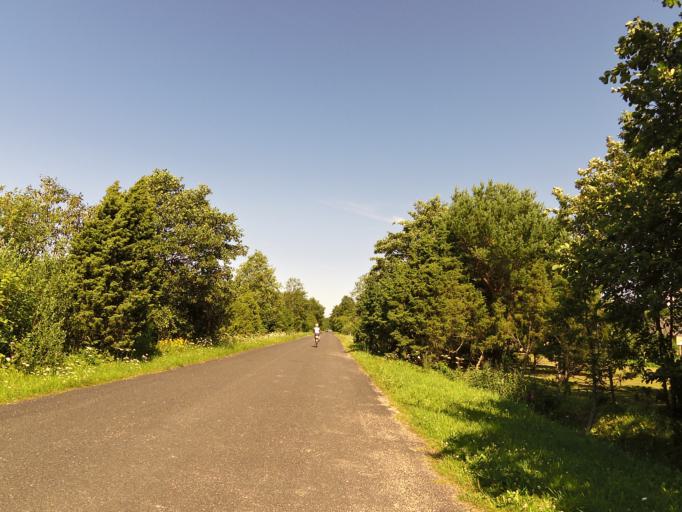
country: EE
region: Hiiumaa
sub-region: Kaerdla linn
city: Kardla
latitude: 58.7808
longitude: 22.4876
